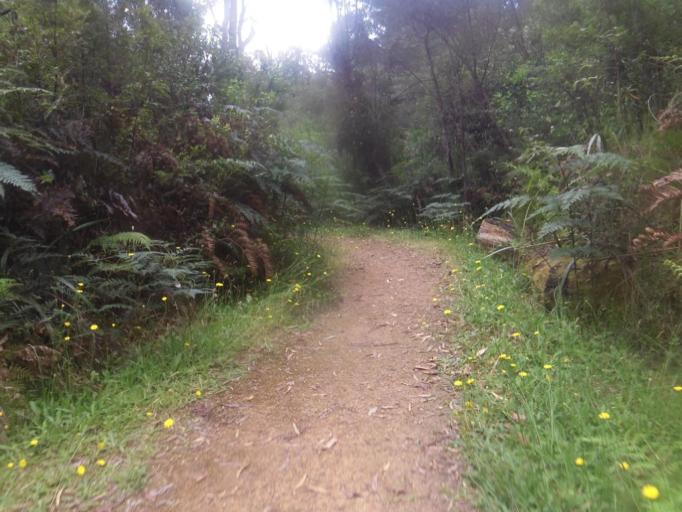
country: AU
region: Victoria
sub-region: Yarra Ranges
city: Millgrove
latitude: -37.5156
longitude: 145.7459
